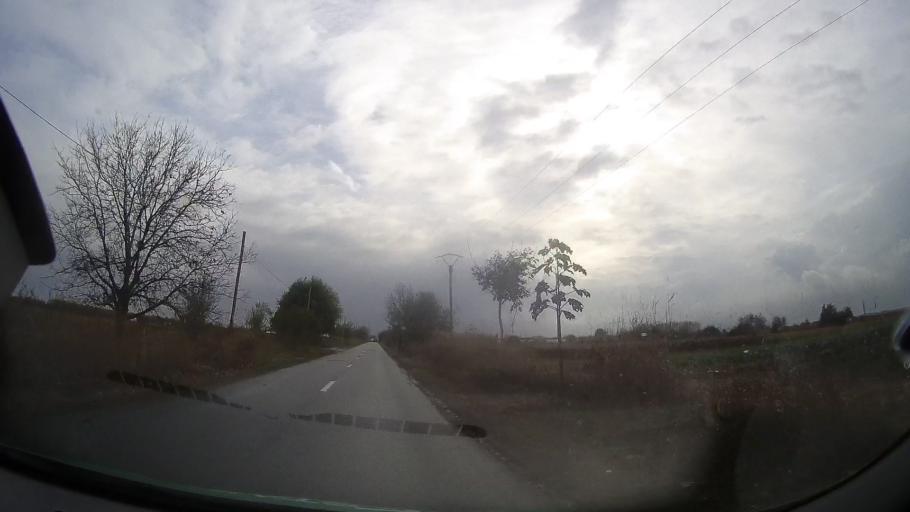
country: RO
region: Ialomita
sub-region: Comuna Fierbinti-Targ
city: Fierbintii de Jos
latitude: 44.7035
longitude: 26.3930
